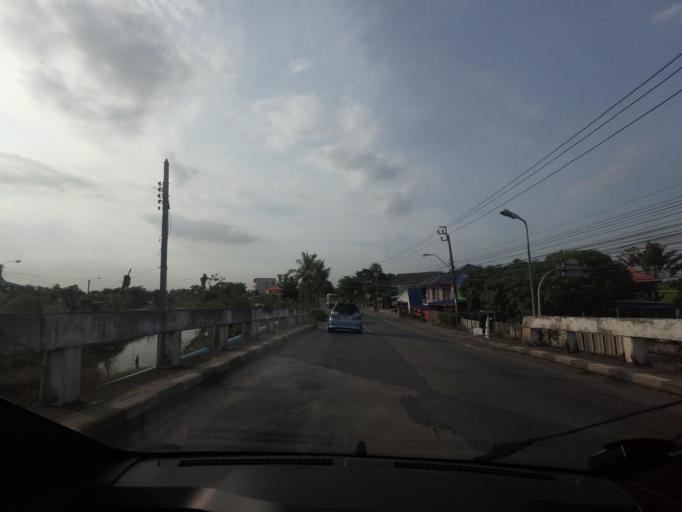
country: TH
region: Bangkok
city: Nong Chok
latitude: 13.8100
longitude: 100.8717
